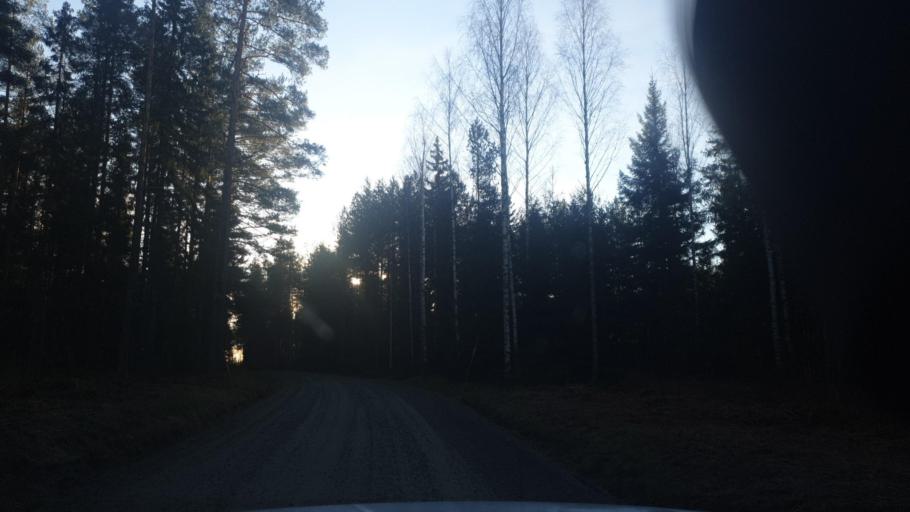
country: SE
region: Vaermland
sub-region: Karlstads Kommun
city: Edsvalla
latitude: 59.6030
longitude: 13.0668
